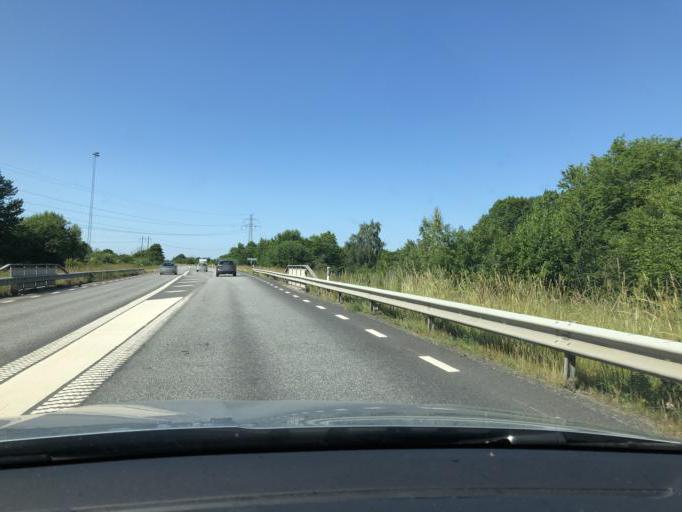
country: SE
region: Skane
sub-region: Bromolla Kommun
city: Bromoella
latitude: 56.0752
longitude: 14.4991
